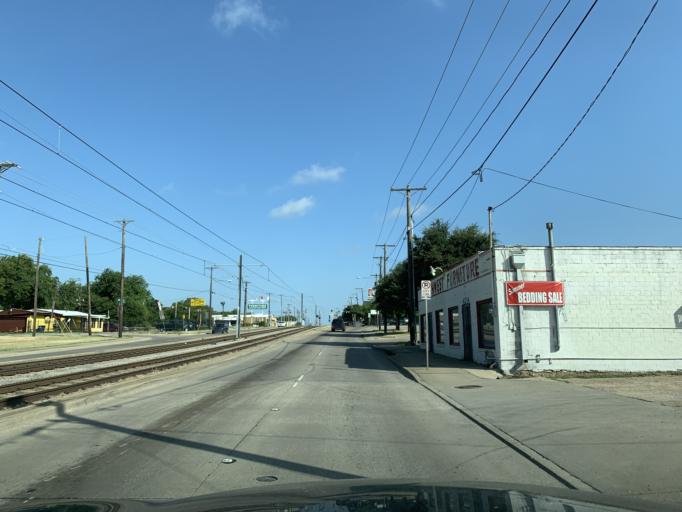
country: US
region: Texas
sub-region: Dallas County
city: Dallas
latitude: 32.6980
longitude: -96.7948
